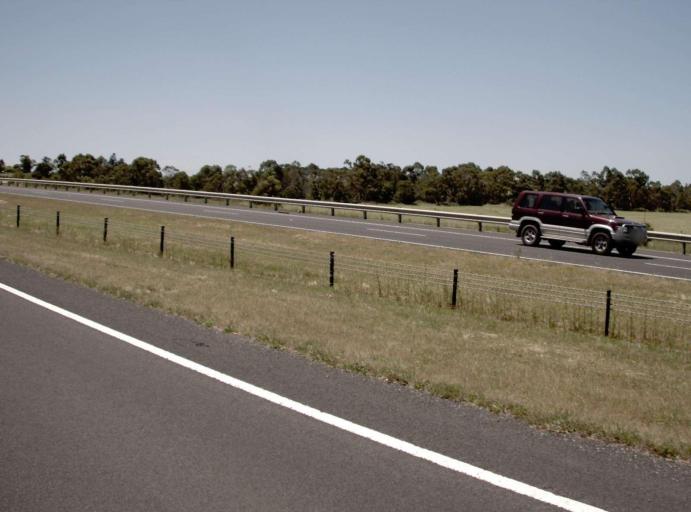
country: AU
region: Victoria
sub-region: Cardinia
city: Pakenham South
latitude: -38.0898
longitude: 145.5017
